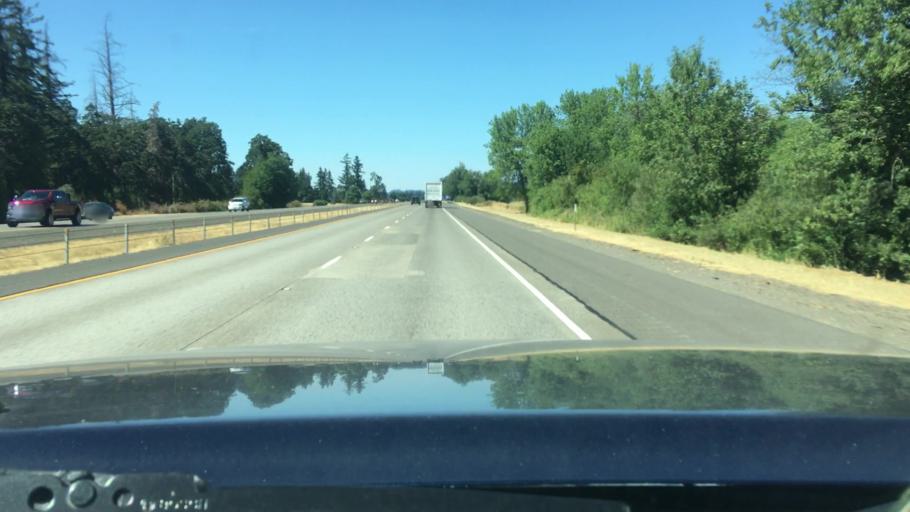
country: US
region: Oregon
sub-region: Lane County
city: Creswell
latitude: 43.8867
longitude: -123.0138
